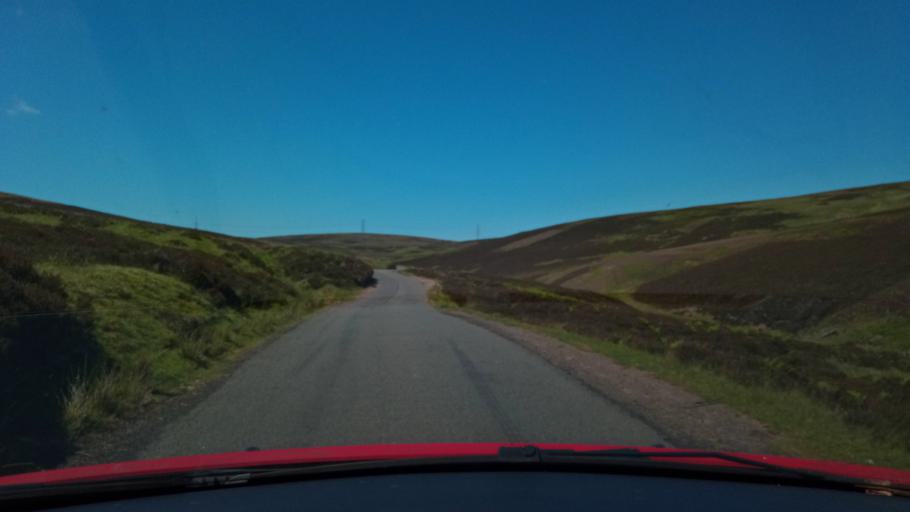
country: GB
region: Scotland
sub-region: East Lothian
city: East Linton
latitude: 55.8482
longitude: -2.5884
